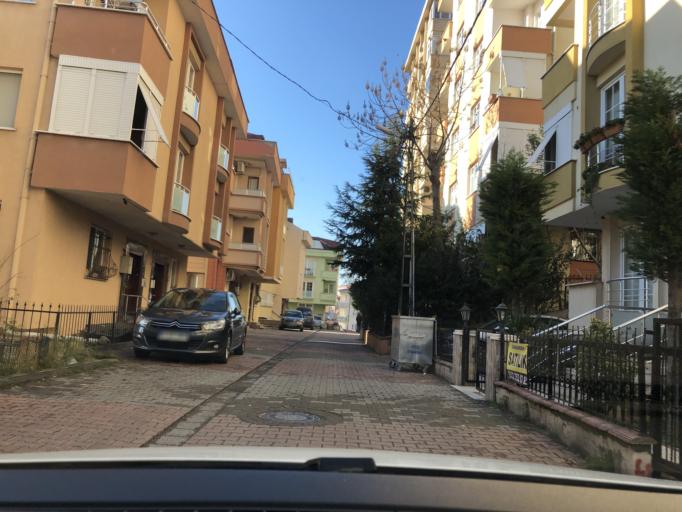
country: TR
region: Istanbul
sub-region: Atasehir
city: Atasehir
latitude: 40.9728
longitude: 29.1232
